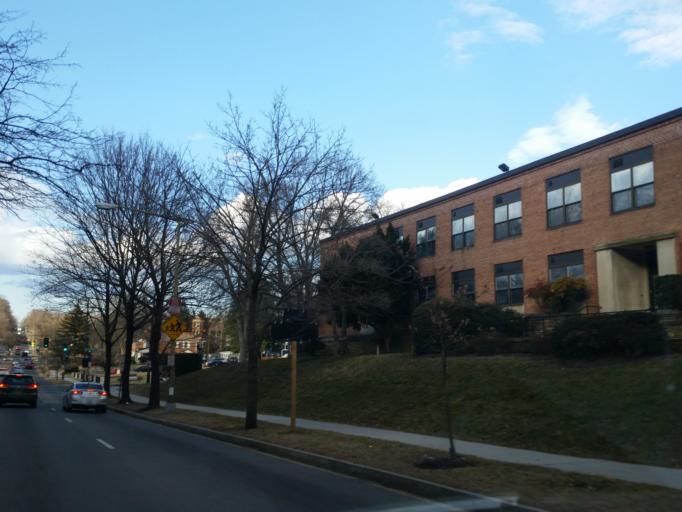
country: US
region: Maryland
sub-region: Montgomery County
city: Silver Spring
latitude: 38.9639
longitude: -77.0363
